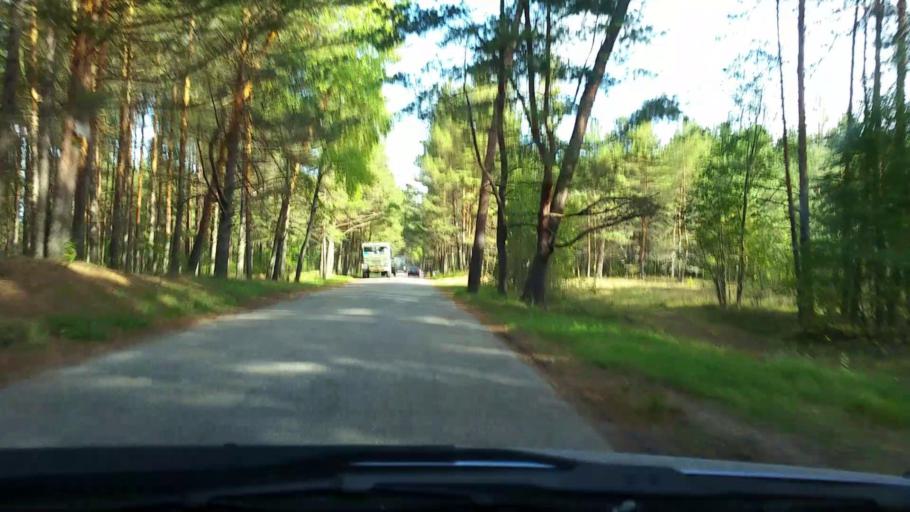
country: LV
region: Adazi
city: Adazi
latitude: 57.0987
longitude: 24.3725
